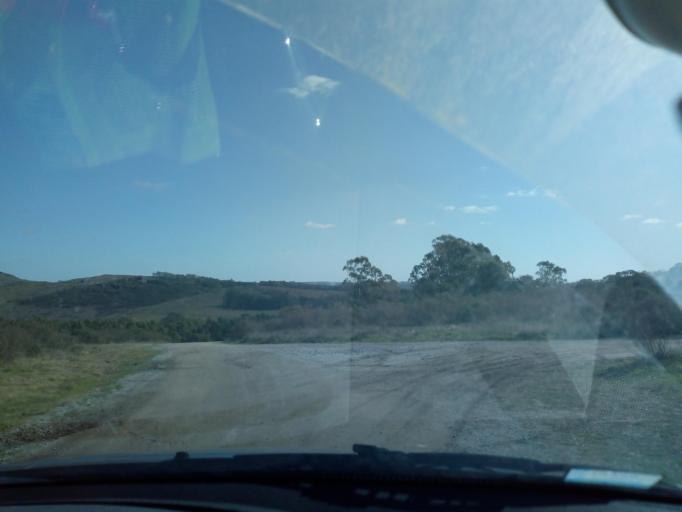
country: AR
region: Buenos Aires
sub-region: Partido de Tandil
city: Tandil
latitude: -37.3640
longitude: -59.1400
